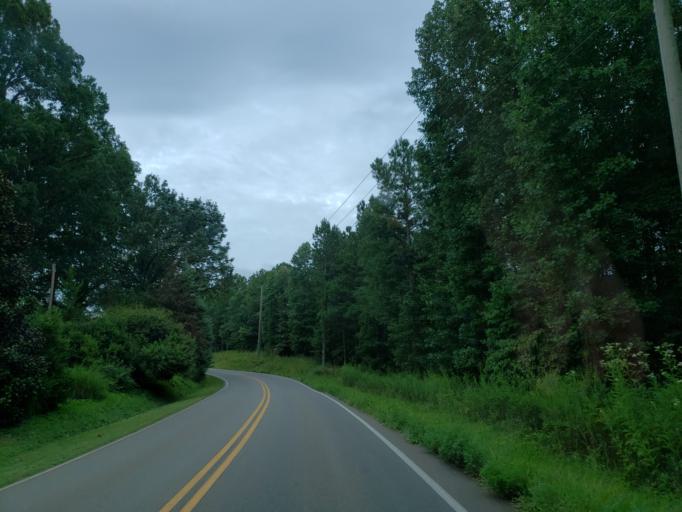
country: US
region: Georgia
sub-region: Pickens County
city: Jasper
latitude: 34.4240
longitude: -84.5826
